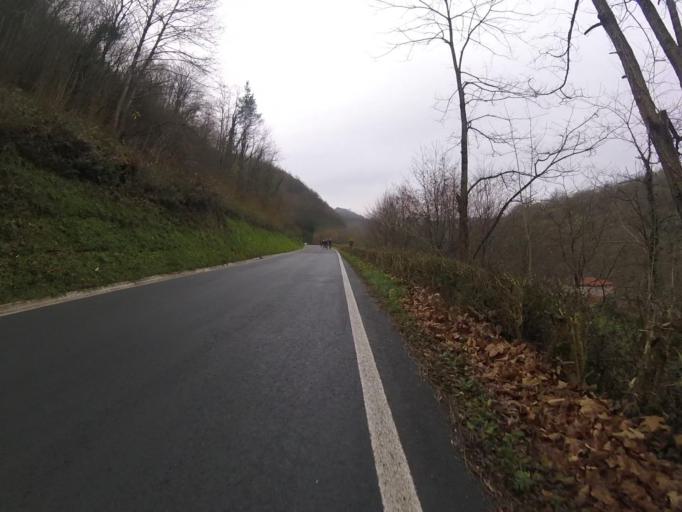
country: ES
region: Navarre
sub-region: Provincia de Navarra
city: Arantza
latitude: 43.2067
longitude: -1.7098
